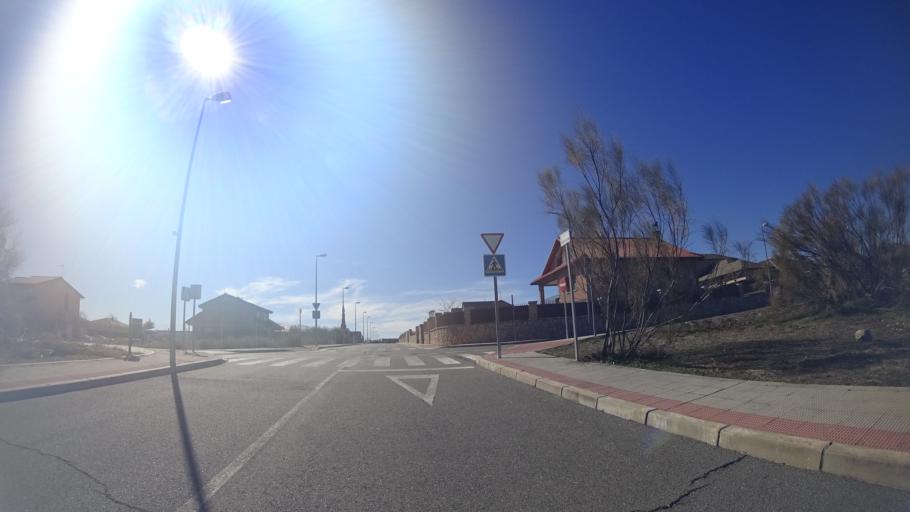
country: ES
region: Madrid
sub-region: Provincia de Madrid
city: Colmenarejo
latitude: 40.5492
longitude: -4.0066
